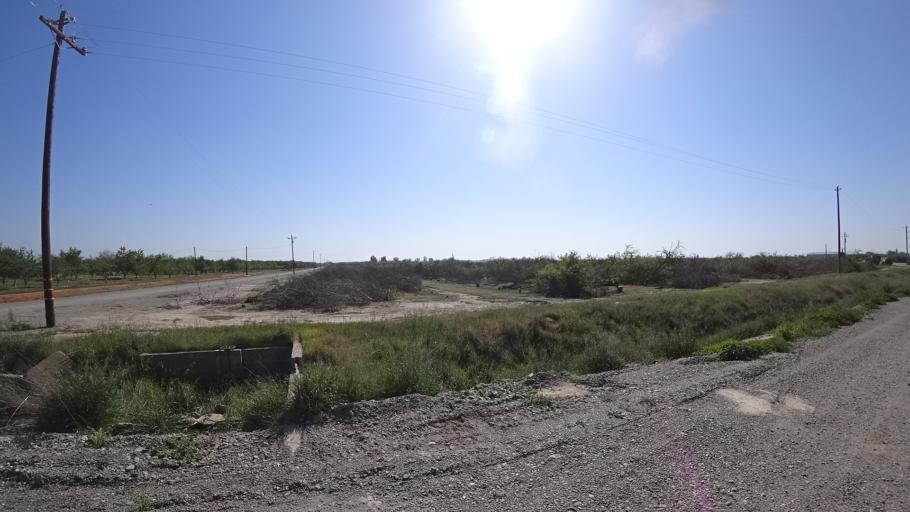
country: US
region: California
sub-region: Glenn County
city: Hamilton City
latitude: 39.6450
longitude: -122.0215
